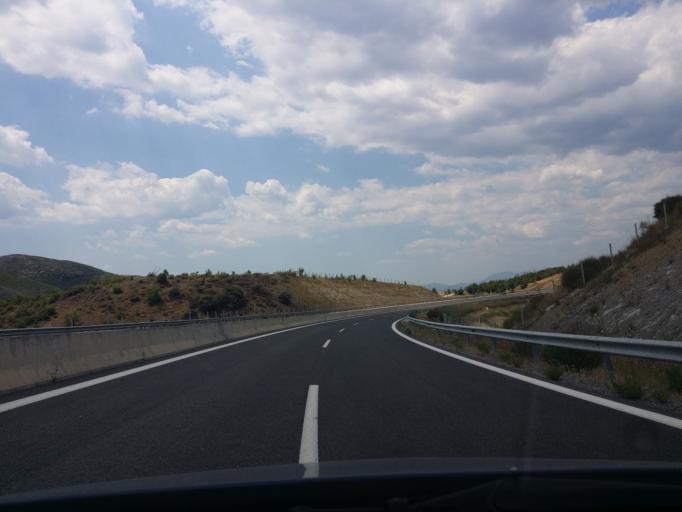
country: GR
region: Peloponnese
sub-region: Nomos Arkadias
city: Megalopoli
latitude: 37.3109
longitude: 22.1714
